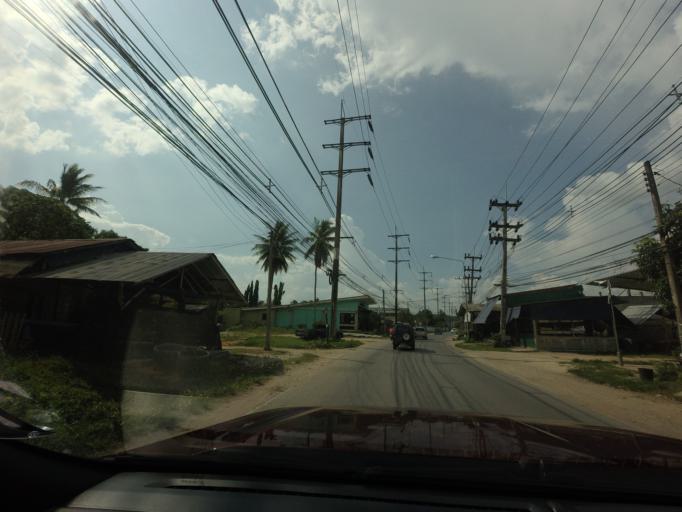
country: TH
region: Yala
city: Yala
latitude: 6.5059
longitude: 101.2693
